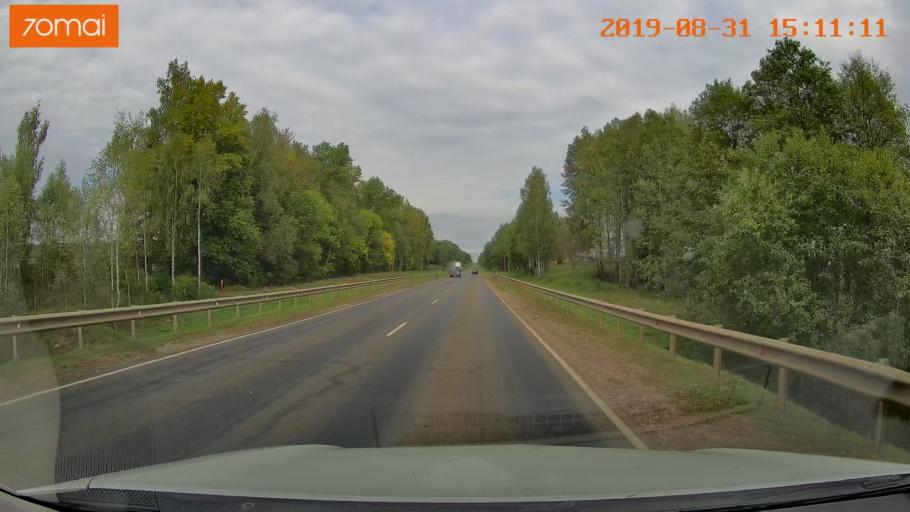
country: RU
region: Kaluga
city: Spas-Demensk
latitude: 54.4204
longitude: 34.2377
